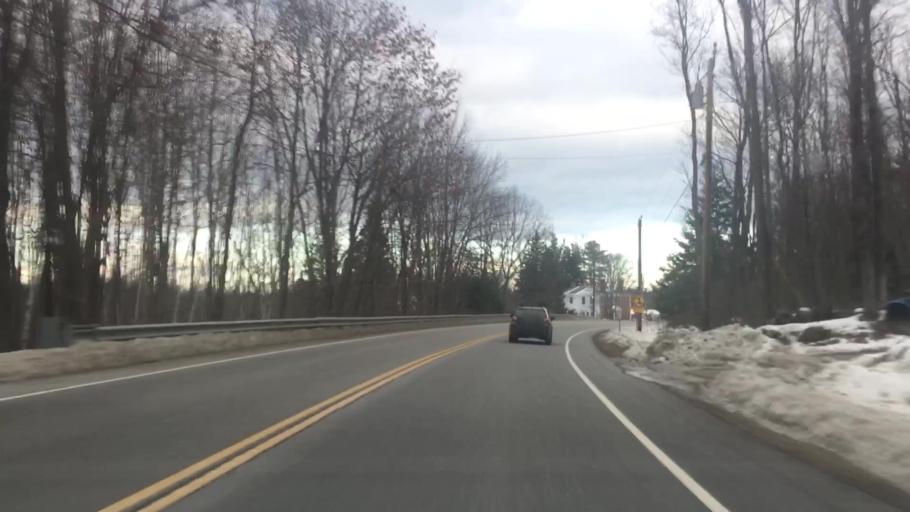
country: US
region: New Hampshire
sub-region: Hillsborough County
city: Antrim
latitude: 43.0806
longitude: -71.9781
